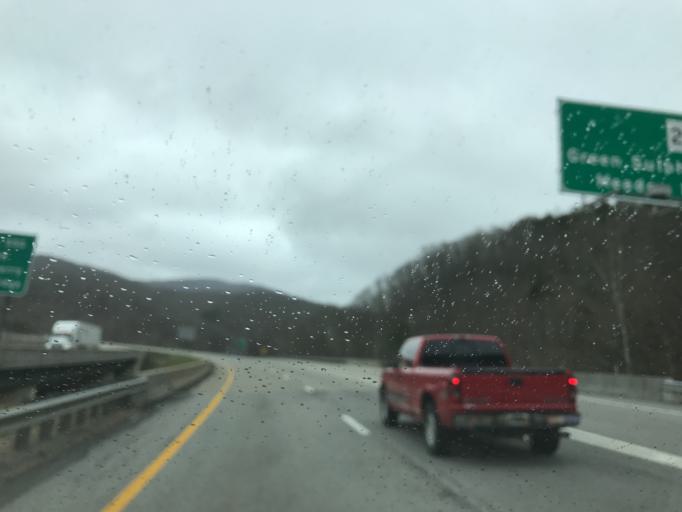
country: US
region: West Virginia
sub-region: Summers County
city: Hinton
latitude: 37.8040
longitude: -80.8203
